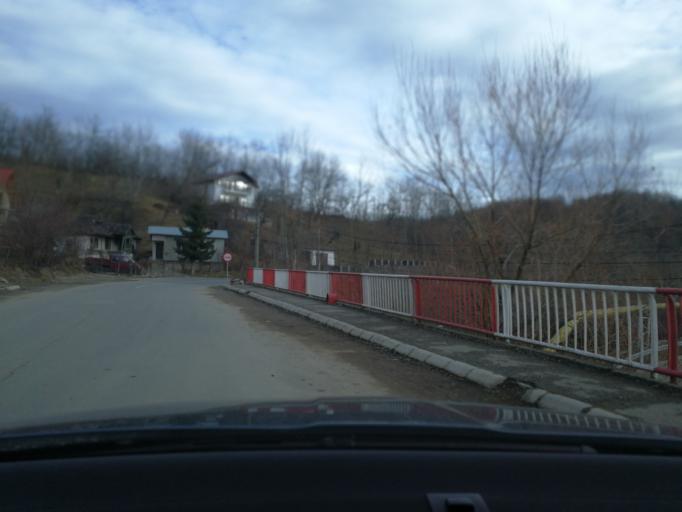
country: RO
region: Prahova
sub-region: Oras Breaza
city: Valea Tarsei
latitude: 45.1814
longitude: 25.6340
